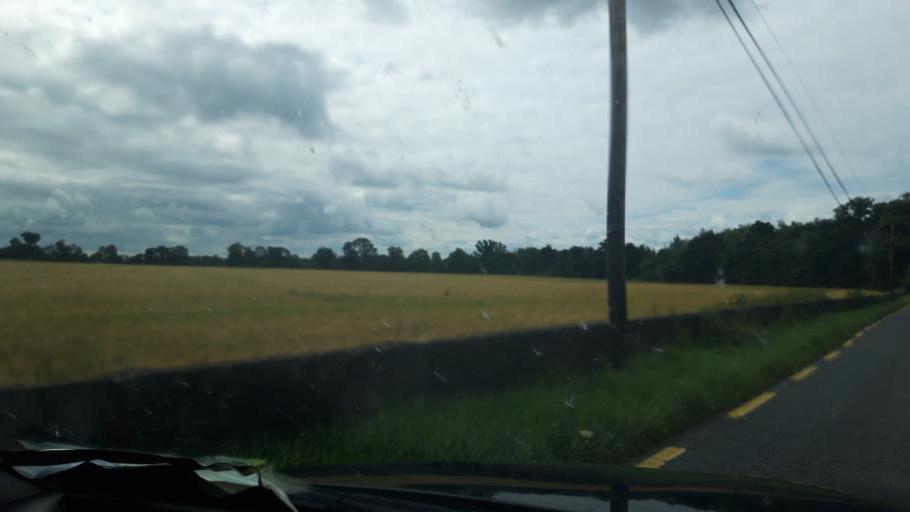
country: IE
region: Leinster
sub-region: Kilkenny
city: Callan
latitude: 52.5814
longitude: -7.3169
